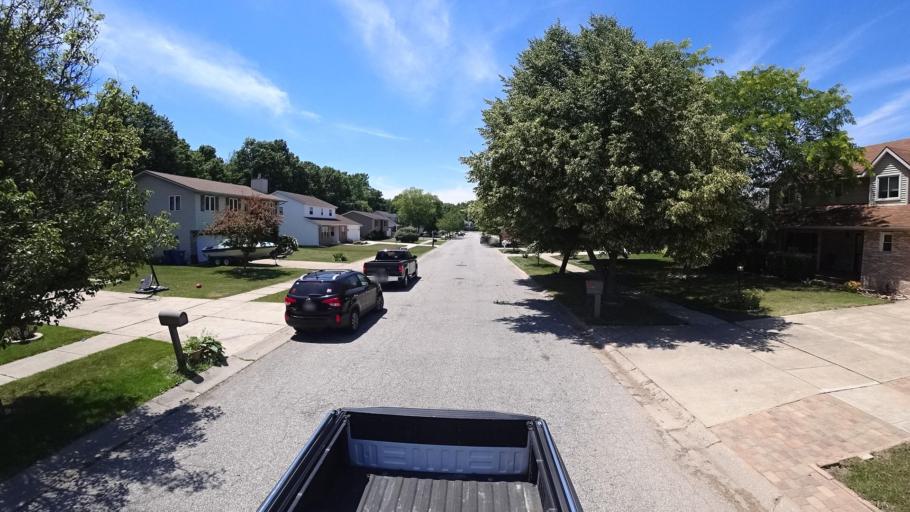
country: US
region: Indiana
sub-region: Porter County
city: Porter
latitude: 41.6026
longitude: -87.0934
